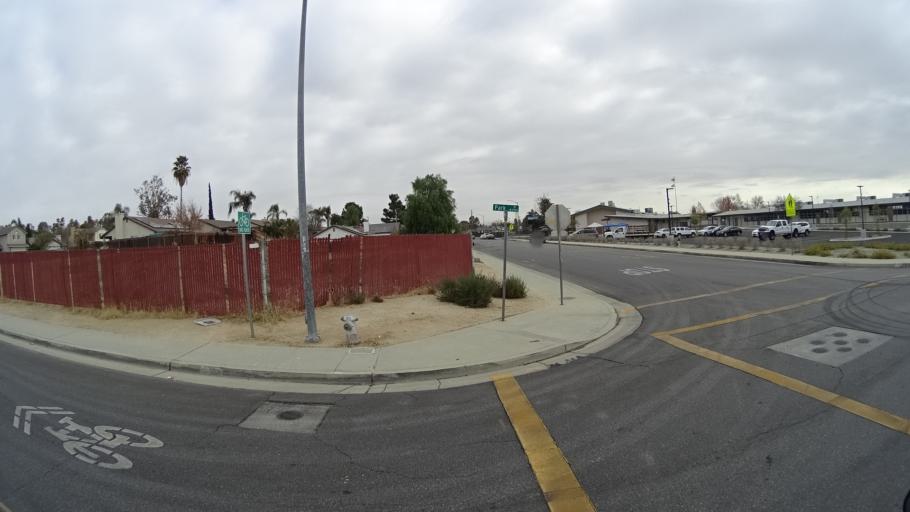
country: US
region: California
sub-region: Kern County
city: Bakersfield
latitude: 35.3798
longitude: -118.9187
